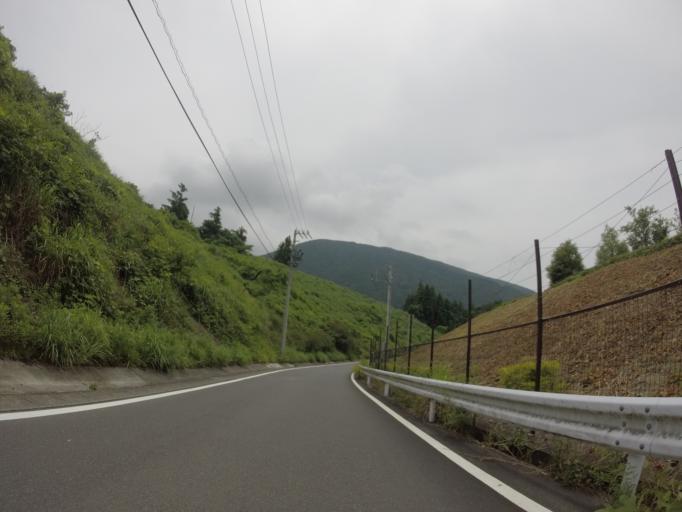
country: JP
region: Shizuoka
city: Fujinomiya
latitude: 35.1336
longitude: 138.5142
